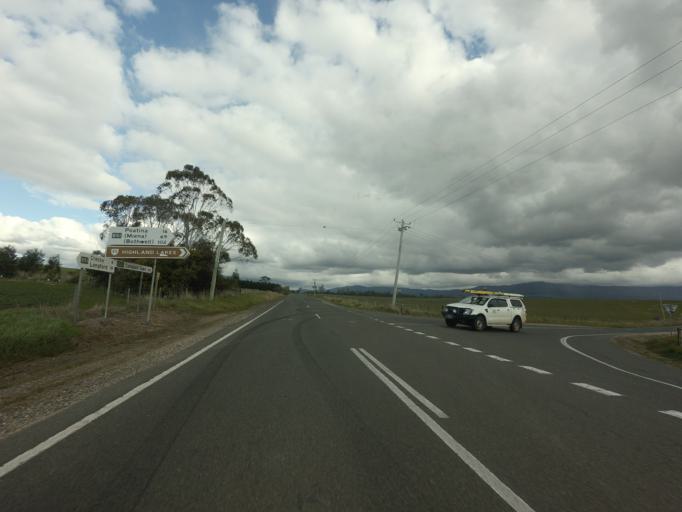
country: AU
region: Tasmania
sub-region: Northern Midlands
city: Longford
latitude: -41.7554
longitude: 147.0825
